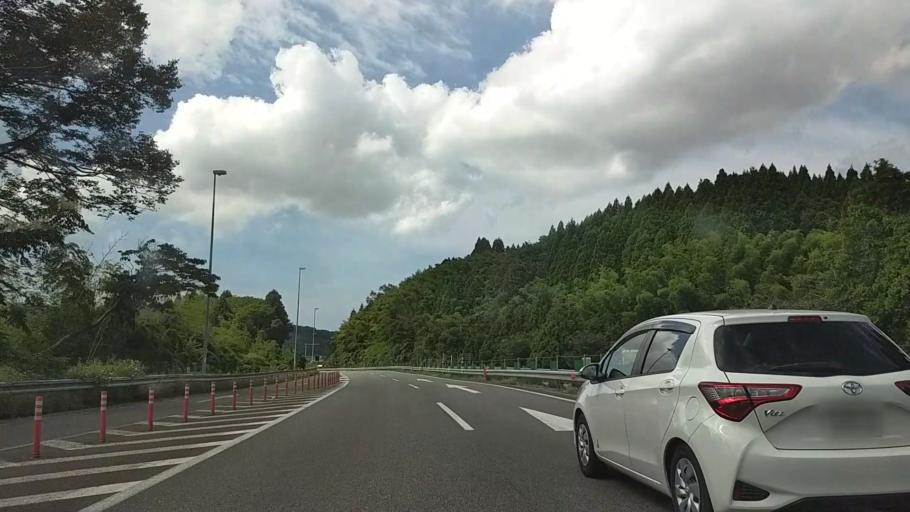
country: JP
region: Ishikawa
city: Tsubata
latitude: 36.6059
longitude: 136.7184
